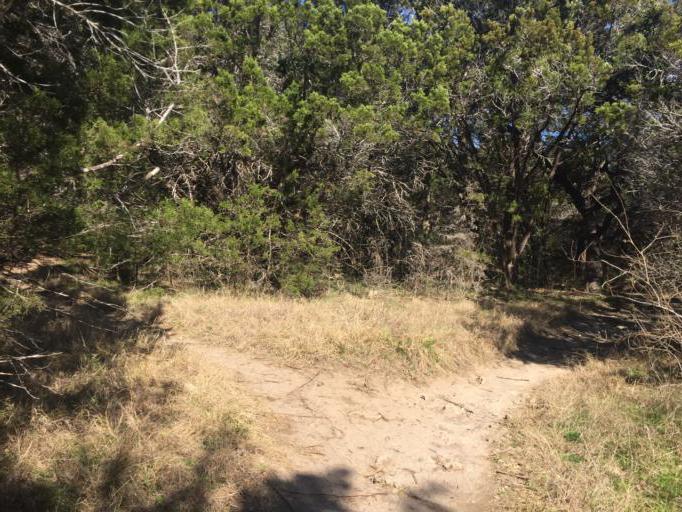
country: US
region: Texas
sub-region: Travis County
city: Onion Creek
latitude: 30.1590
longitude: -97.8057
